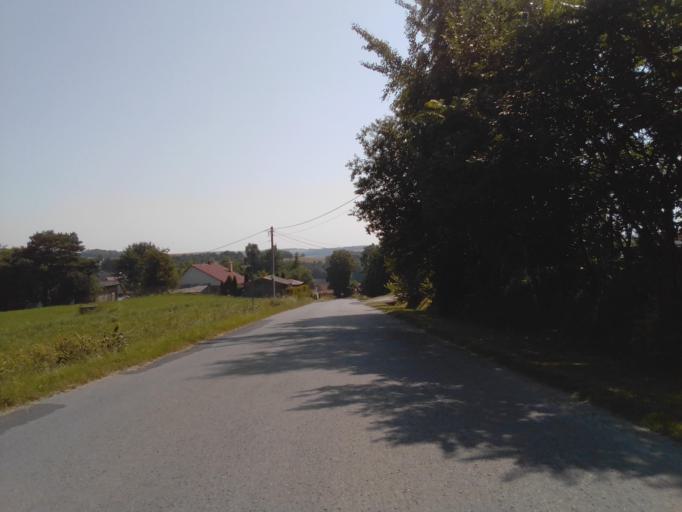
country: PL
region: Subcarpathian Voivodeship
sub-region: Powiat ropczycko-sedziszowski
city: Zagorzyce
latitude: 50.0103
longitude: 21.6316
